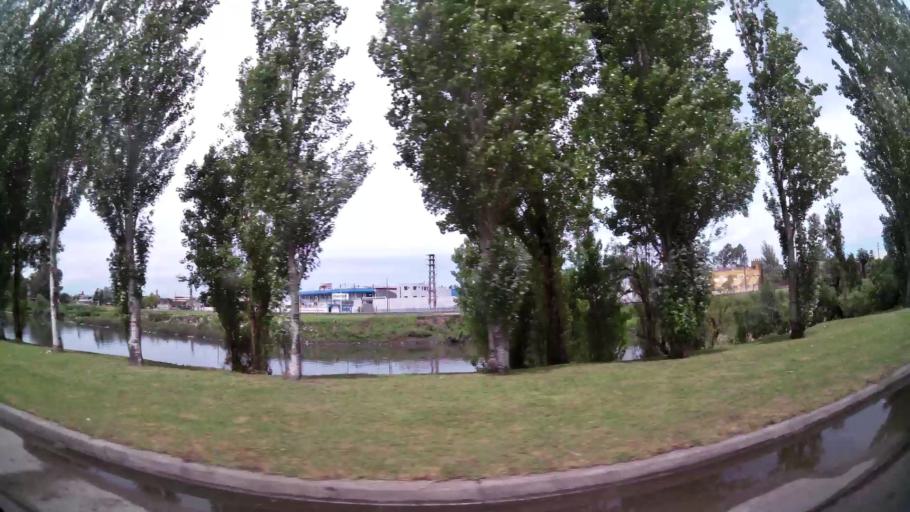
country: AR
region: Buenos Aires F.D.
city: Villa Lugano
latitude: -34.6823
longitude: -58.4422
